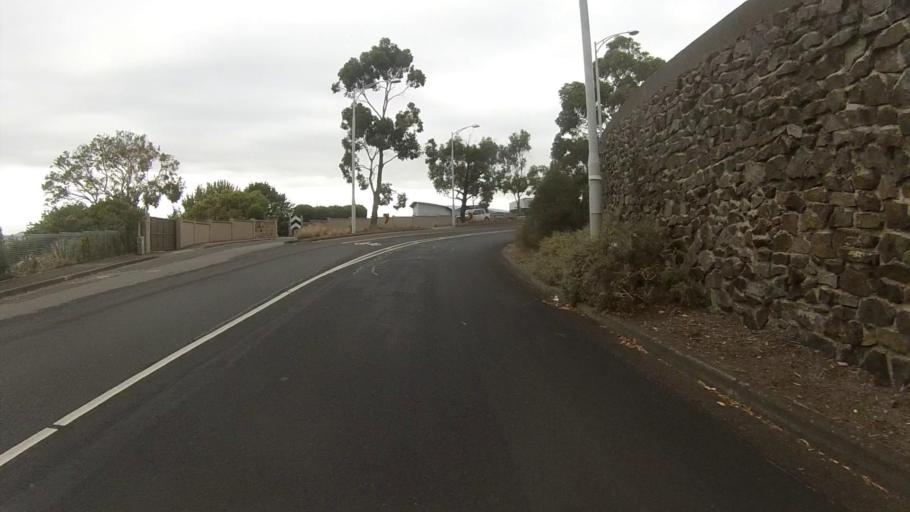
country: AU
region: Tasmania
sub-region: Kingborough
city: Taroona
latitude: -42.9140
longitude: 147.3579
